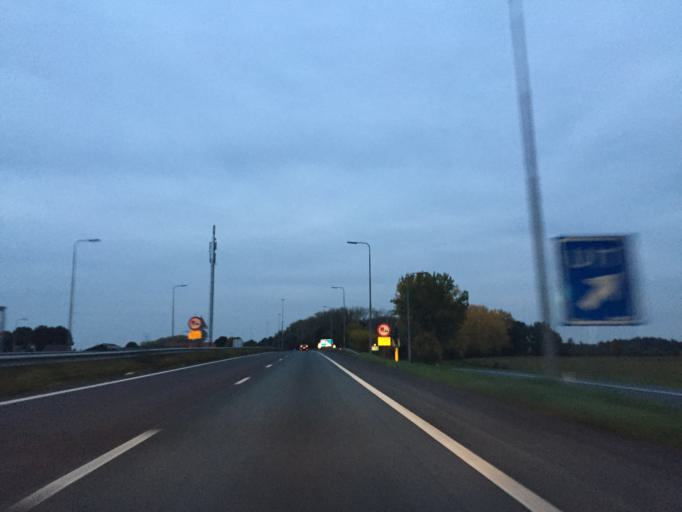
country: NL
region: North Brabant
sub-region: Gemeente Waalwijk
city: Waalwijk
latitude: 51.6936
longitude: 5.1082
